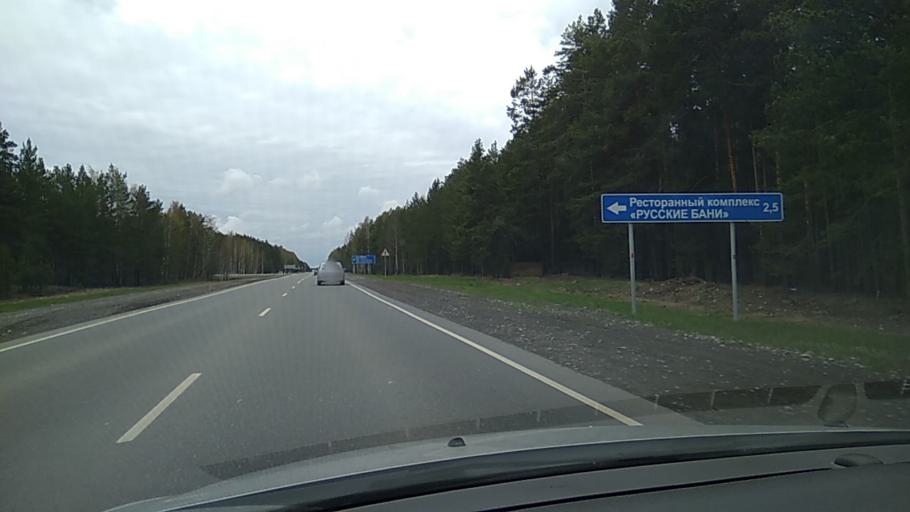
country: RU
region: Tjumen
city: Chervishevo
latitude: 56.9910
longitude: 65.4722
